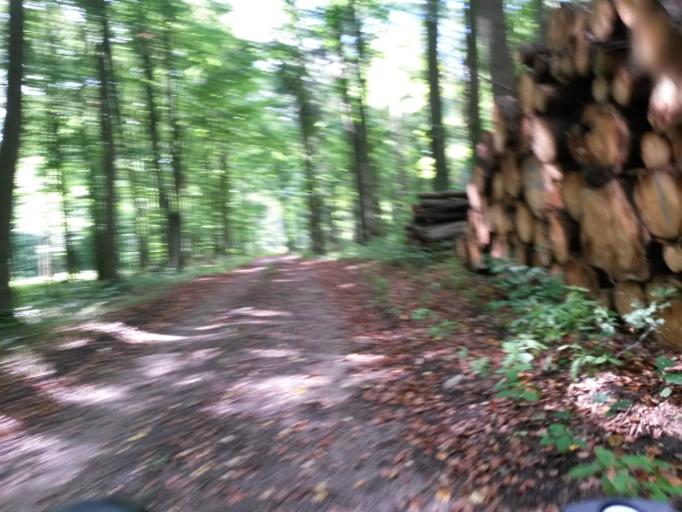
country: DE
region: Brandenburg
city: Milmersdorf
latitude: 53.1366
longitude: 13.5781
